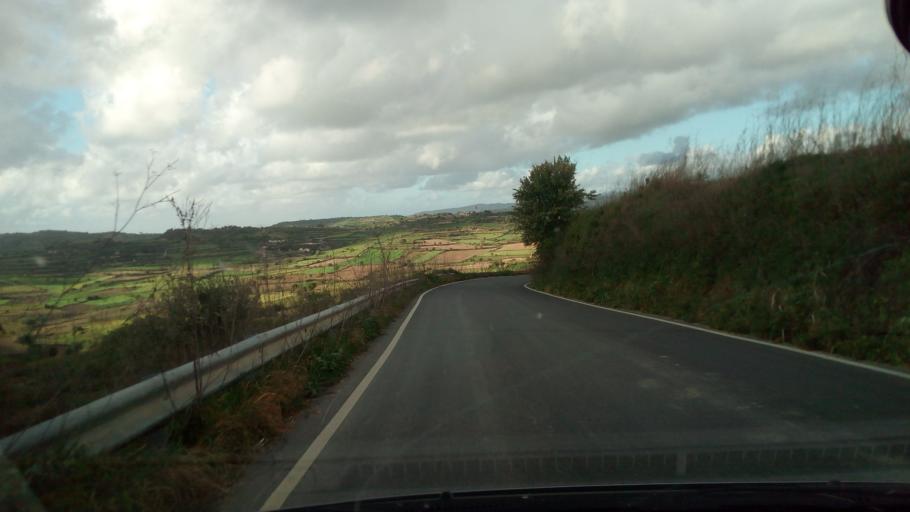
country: CY
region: Pafos
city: Mesogi
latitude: 34.8633
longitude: 32.5021
